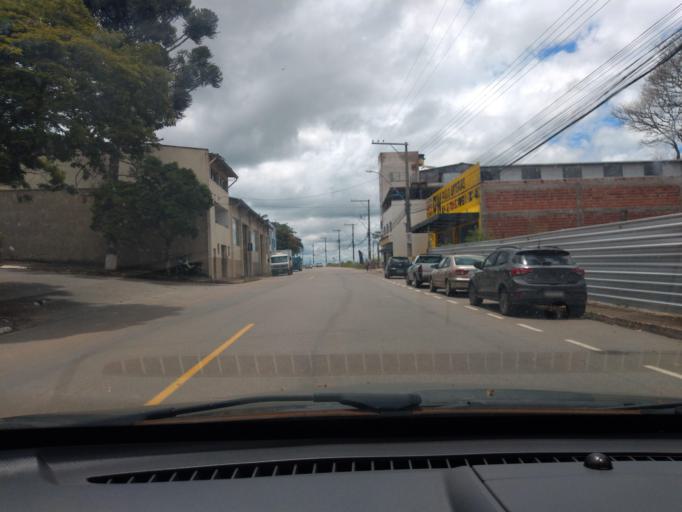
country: BR
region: Minas Gerais
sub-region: Lavras
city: Lavras
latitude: -21.2420
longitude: -45.0220
